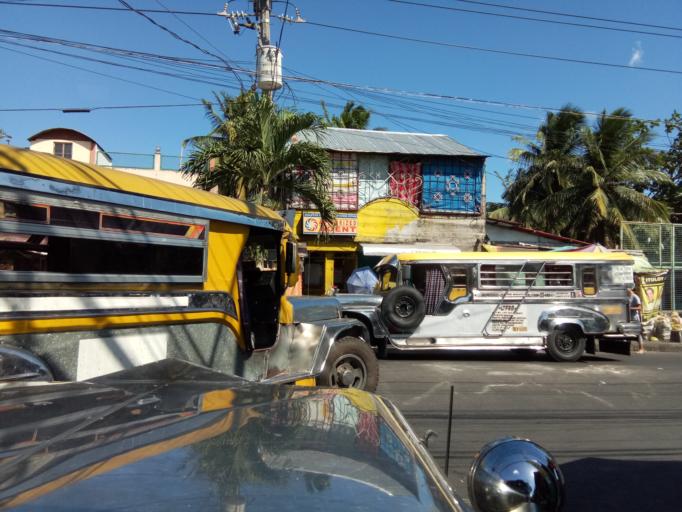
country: PH
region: Calabarzon
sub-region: Province of Cavite
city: Dasmarinas
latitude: 14.3374
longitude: 120.9553
